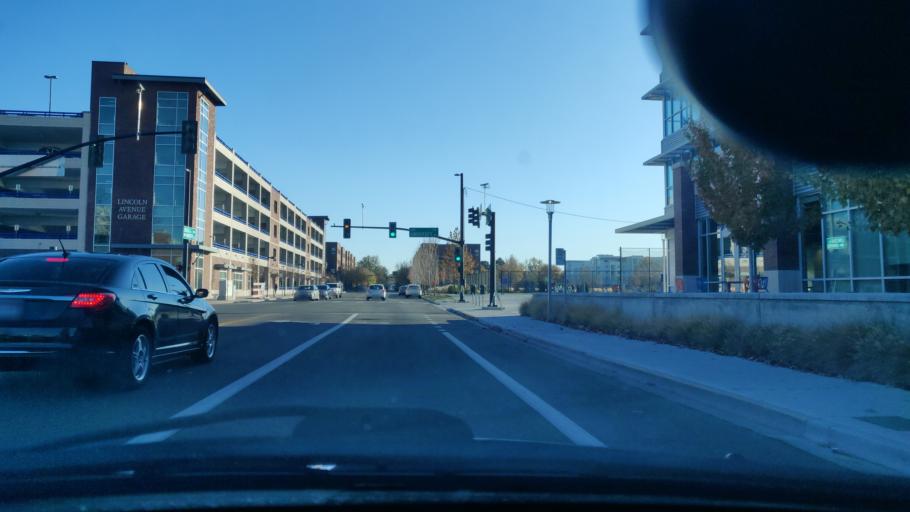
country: US
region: Idaho
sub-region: Ada County
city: Boise
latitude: 43.6014
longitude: -116.2024
